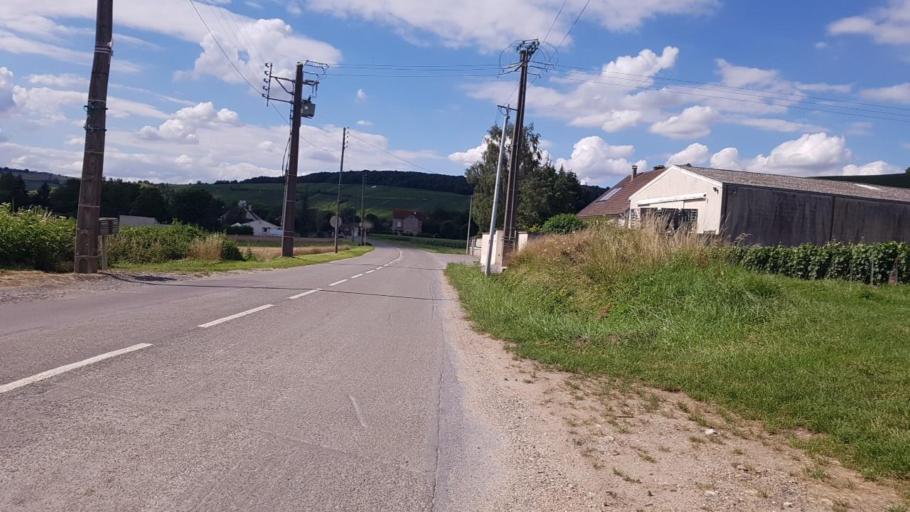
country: FR
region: Picardie
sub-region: Departement de l'Aisne
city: Crezancy
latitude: 49.0755
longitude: 3.5618
